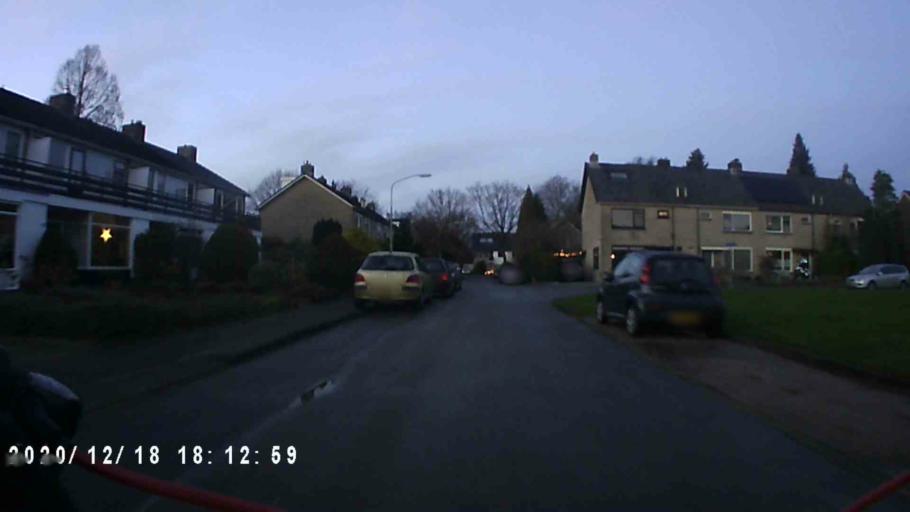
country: NL
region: Groningen
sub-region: Gemeente Haren
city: Haren
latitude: 53.1465
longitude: 6.5566
